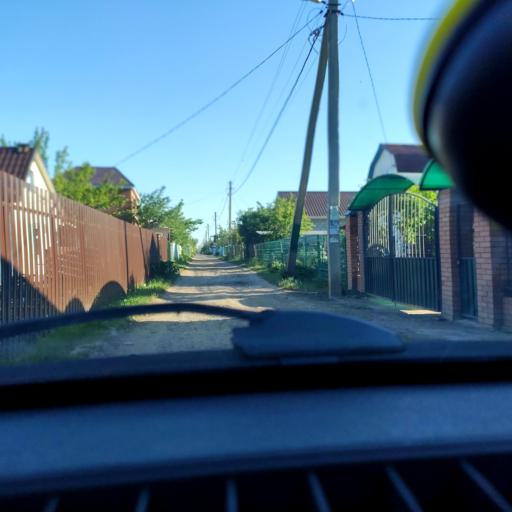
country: RU
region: Samara
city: Tol'yatti
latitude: 53.5978
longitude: 49.3163
